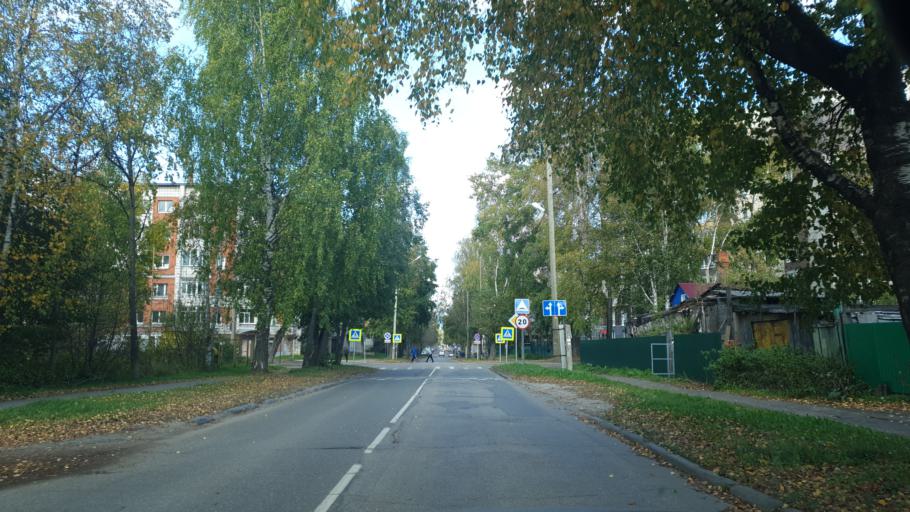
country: RU
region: Komi Republic
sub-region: Syktyvdinskiy Rayon
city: Syktyvkar
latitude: 61.6619
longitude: 50.8416
